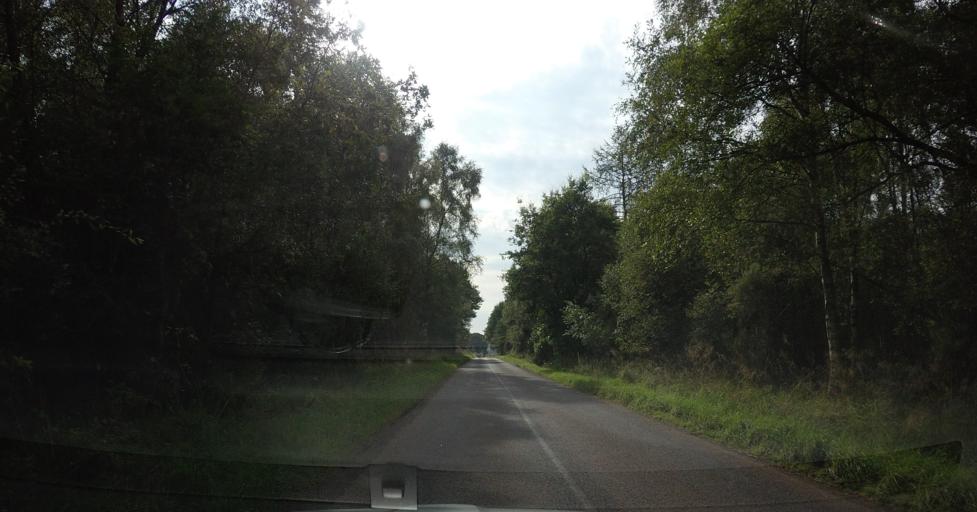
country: GB
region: Scotland
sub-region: Perth and Kinross
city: Auchterarder
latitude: 56.3511
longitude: -3.7274
